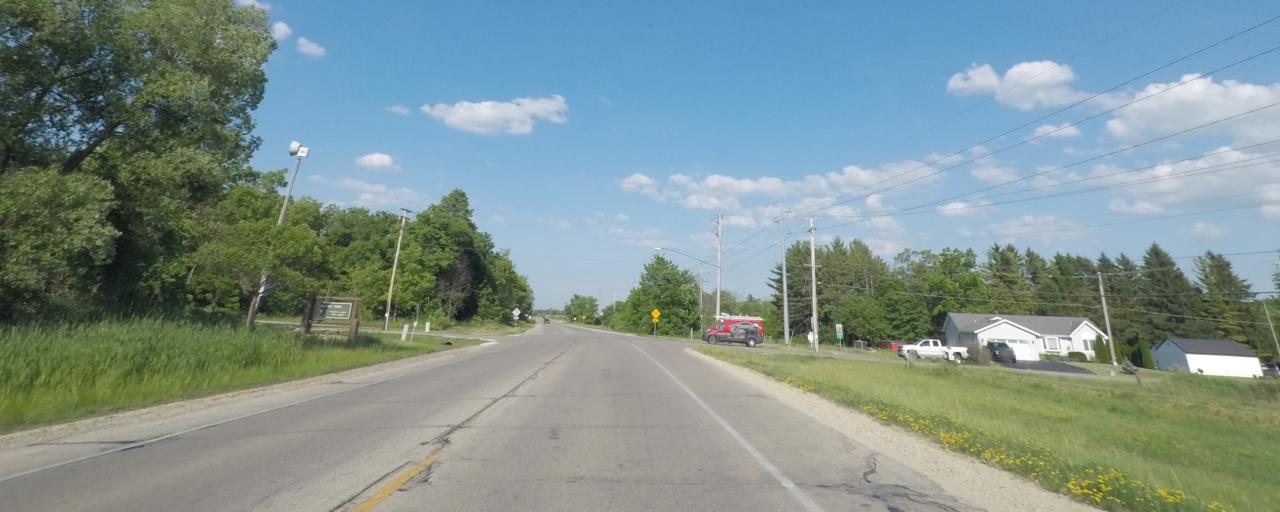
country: US
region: Wisconsin
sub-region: Waukesha County
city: Muskego
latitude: 42.8938
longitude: -88.1653
